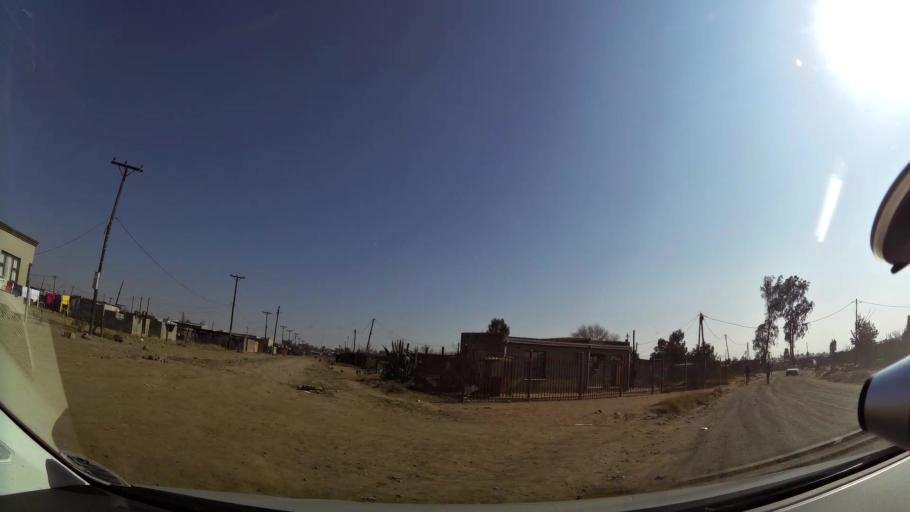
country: ZA
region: Orange Free State
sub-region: Mangaung Metropolitan Municipality
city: Bloemfontein
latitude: -29.1737
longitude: 26.2907
